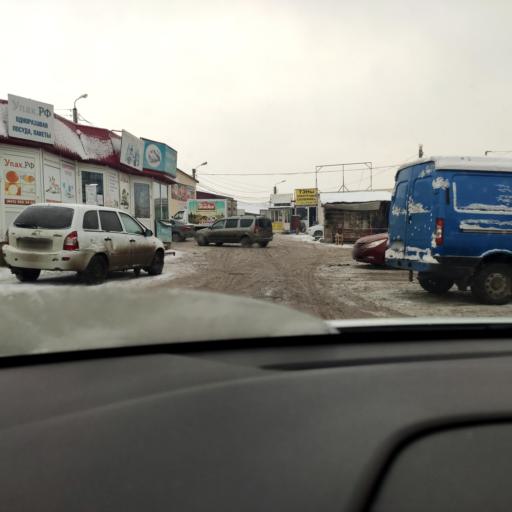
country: RU
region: Tatarstan
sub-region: Gorod Kazan'
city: Kazan
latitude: 55.7713
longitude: 49.1771
